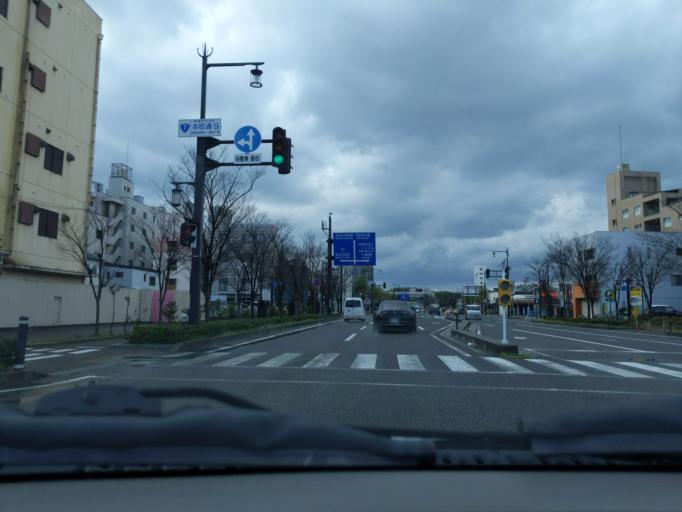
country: JP
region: Niigata
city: Niigata-shi
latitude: 37.9258
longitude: 139.0481
